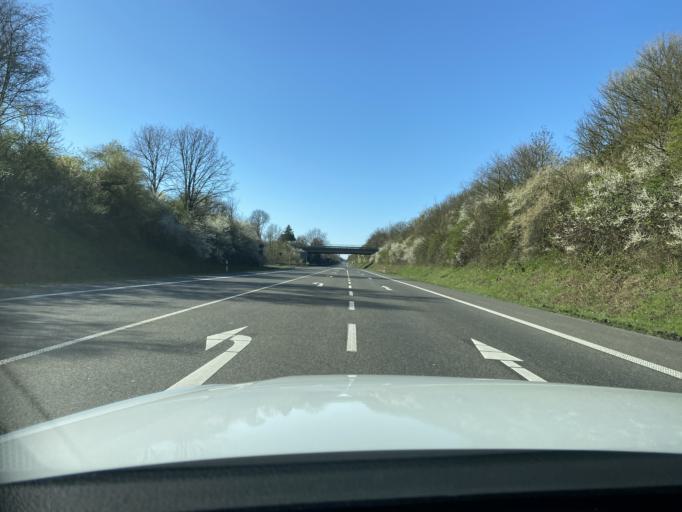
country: DE
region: North Rhine-Westphalia
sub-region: Regierungsbezirk Dusseldorf
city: Neubrueck
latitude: 51.1040
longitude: 6.6280
